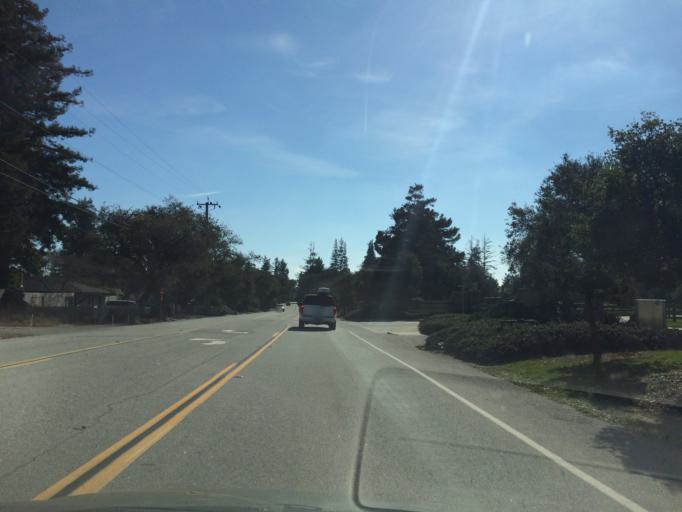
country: US
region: California
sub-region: Santa Cruz County
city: Pasatiempo
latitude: 37.0098
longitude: -122.0342
